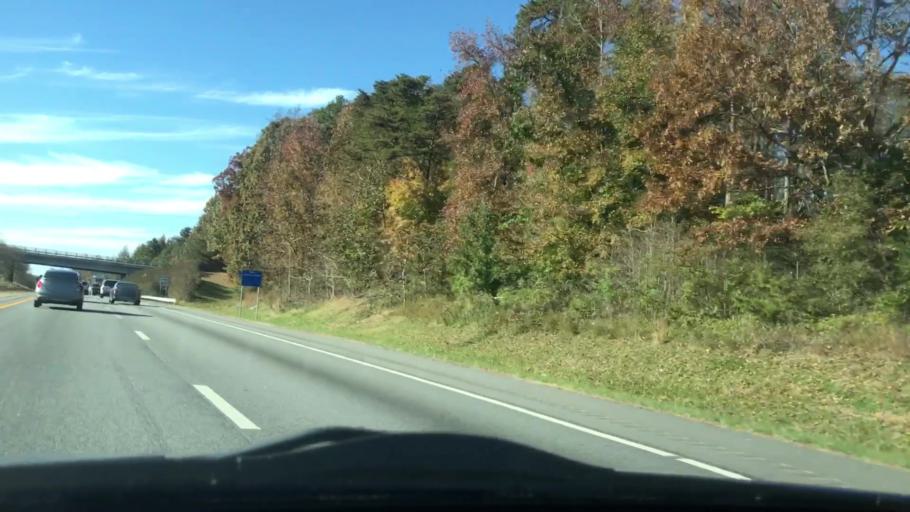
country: US
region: North Carolina
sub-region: Guilford County
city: High Point
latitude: 36.0072
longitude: -80.0007
